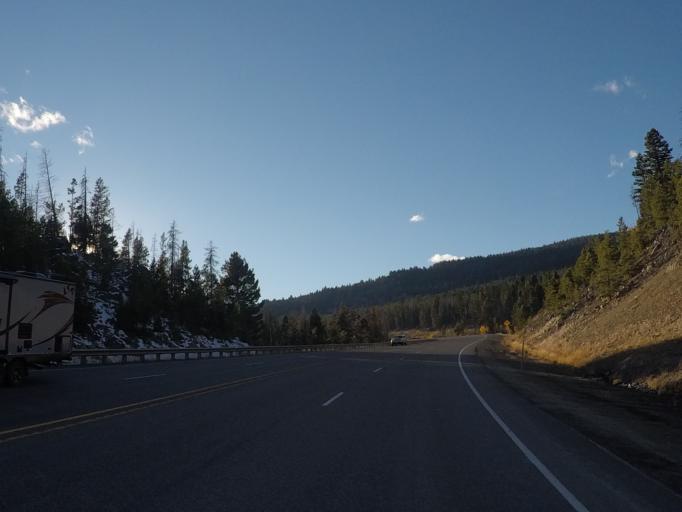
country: US
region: Montana
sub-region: Lewis and Clark County
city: Helena West Side
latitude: 46.5760
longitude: -112.2849
